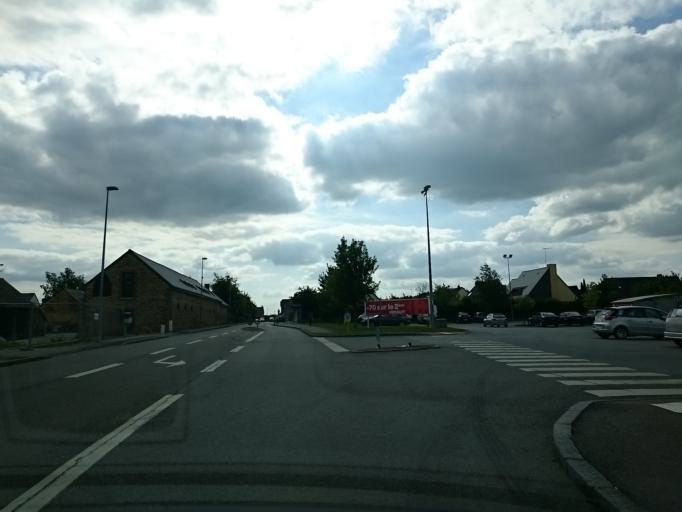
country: FR
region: Brittany
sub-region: Departement d'Ille-et-Vilaine
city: Laille
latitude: 47.9787
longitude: -1.7121
